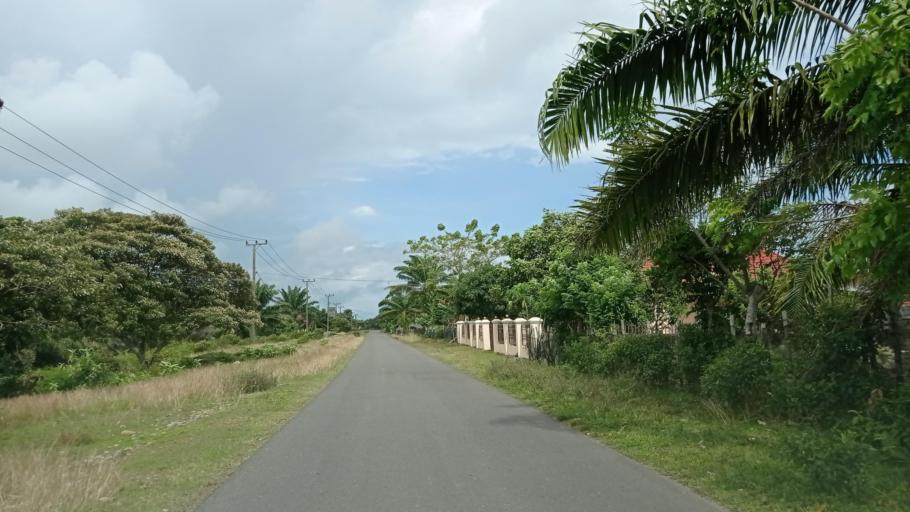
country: ID
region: Bengkulu
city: Ipuh
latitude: -2.5655
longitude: 101.1137
